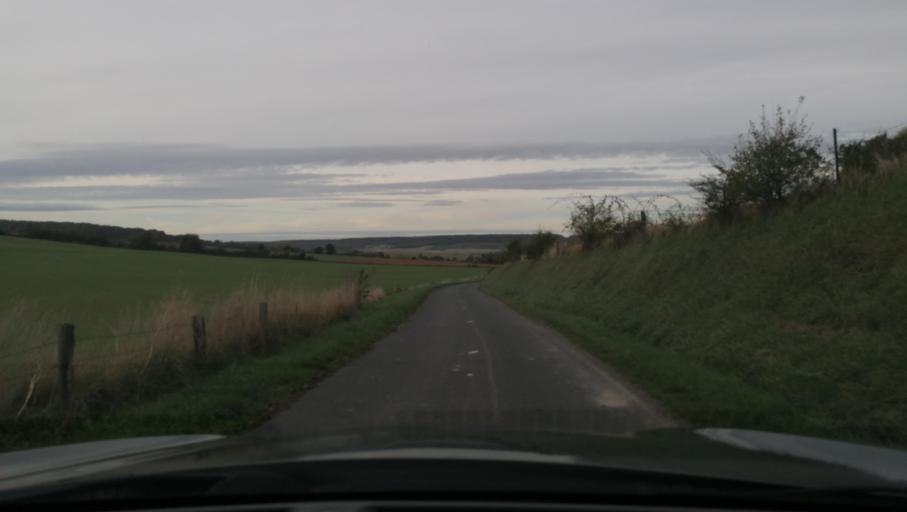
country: FR
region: Picardie
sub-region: Departement de la Somme
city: Bouttencourt
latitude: 49.8921
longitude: 1.6741
